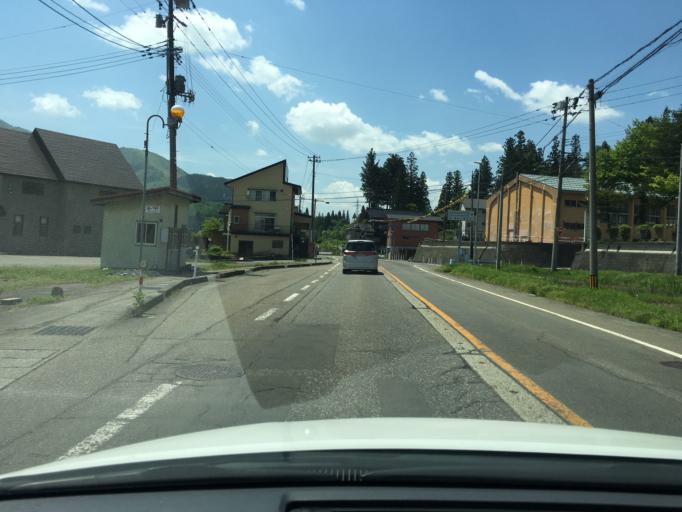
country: JP
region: Niigata
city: Tochio-honcho
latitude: 37.3174
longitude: 139.0150
